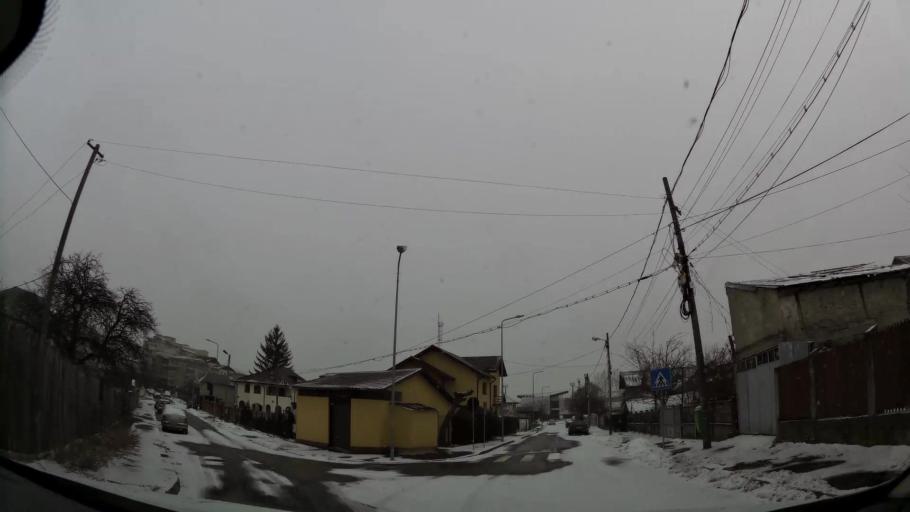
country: RO
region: Dambovita
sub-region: Municipiul Targoviste
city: Targoviste
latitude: 44.9162
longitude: 25.4622
